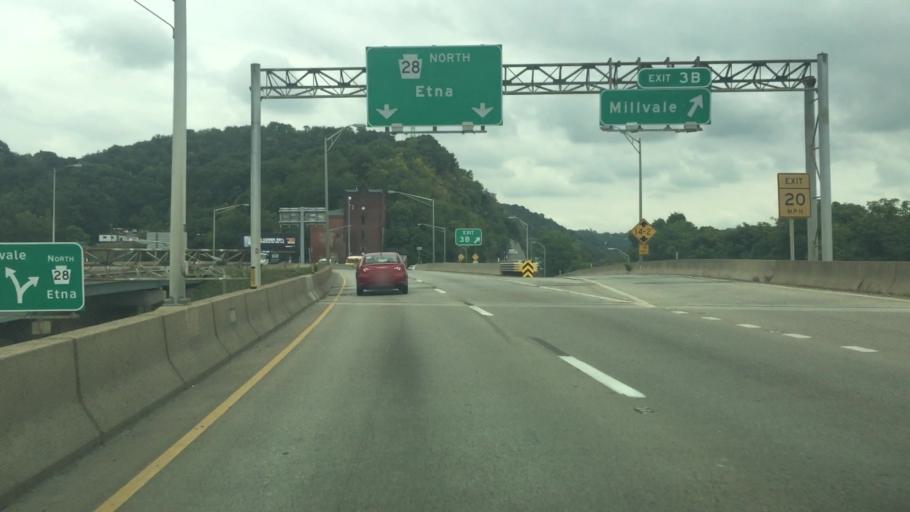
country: US
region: Pennsylvania
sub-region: Allegheny County
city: Millvale
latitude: 40.4769
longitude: -79.9689
